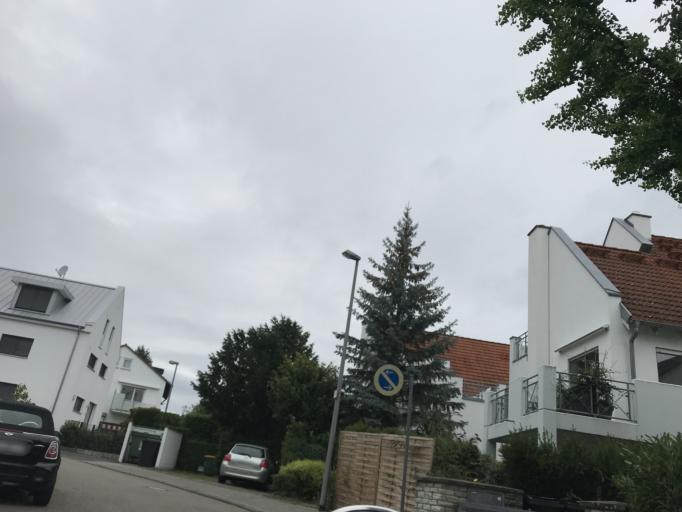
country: DE
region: Hesse
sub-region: Regierungsbezirk Darmstadt
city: Wiesbaden
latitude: 50.0918
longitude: 8.2306
